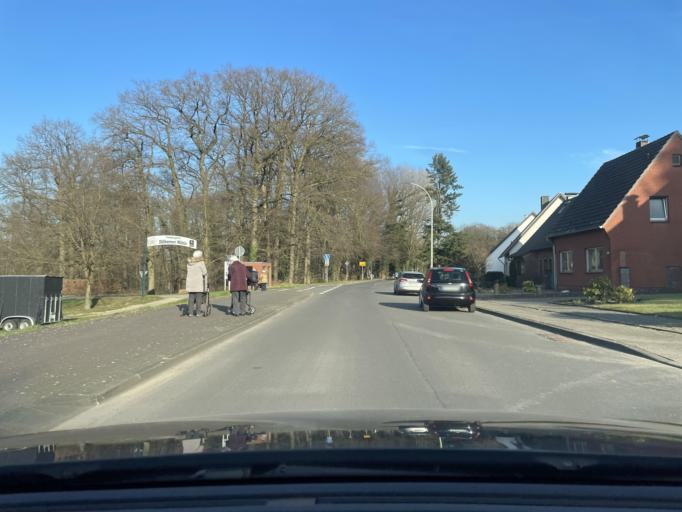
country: DE
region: North Rhine-Westphalia
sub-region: Regierungsbezirk Dusseldorf
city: Bruggen
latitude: 51.2336
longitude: 6.1640
